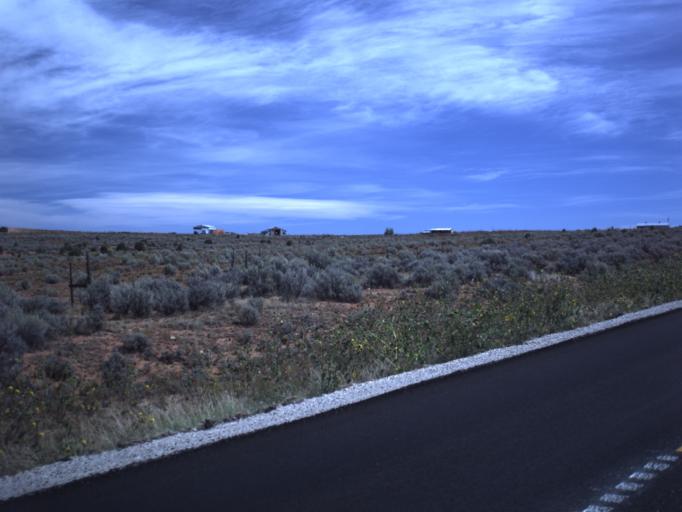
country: US
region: Utah
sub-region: San Juan County
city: Blanding
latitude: 37.5738
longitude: -109.4990
